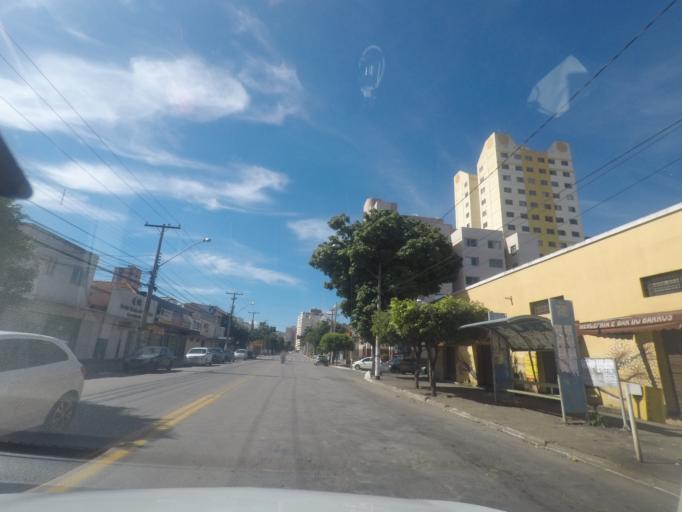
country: BR
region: Goias
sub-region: Goiania
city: Goiania
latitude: -16.6684
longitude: -49.2623
